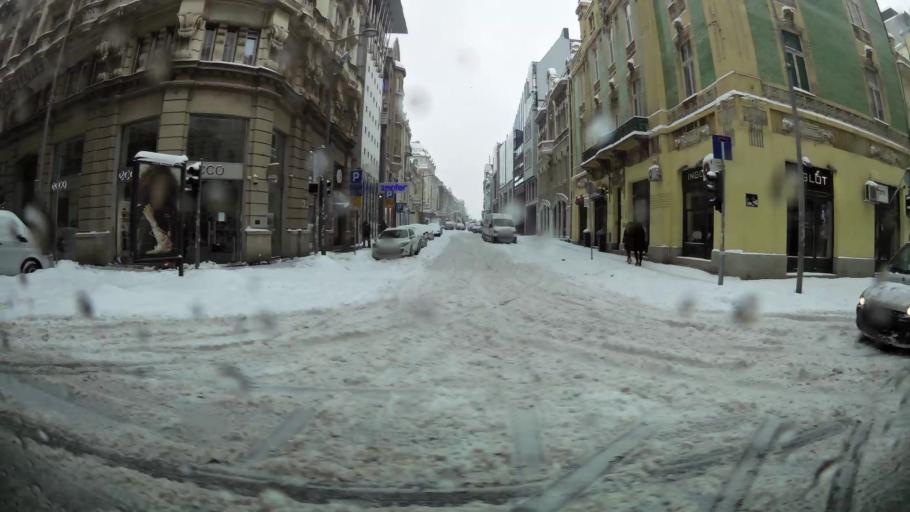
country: RS
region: Central Serbia
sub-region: Belgrade
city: Stari Grad
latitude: 44.8202
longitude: 20.4555
